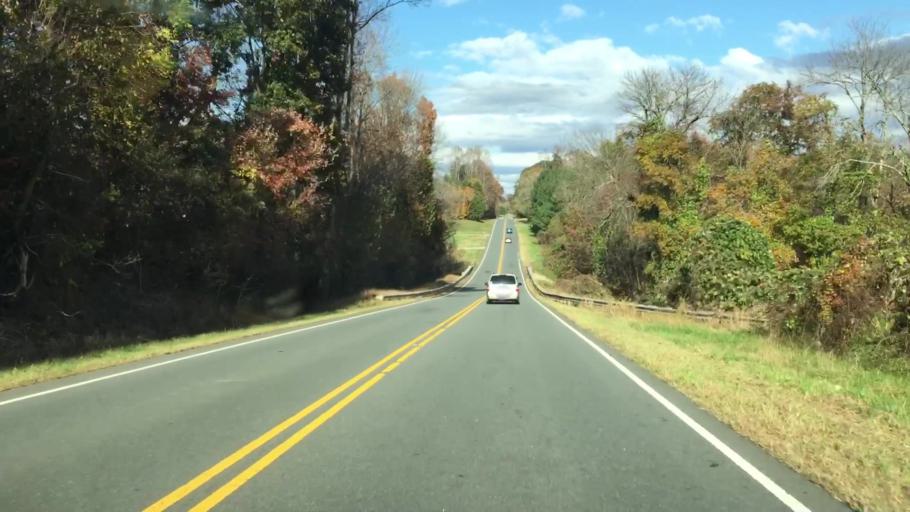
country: US
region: North Carolina
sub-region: Forsyth County
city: Walkertown
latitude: 36.2050
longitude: -80.0742
